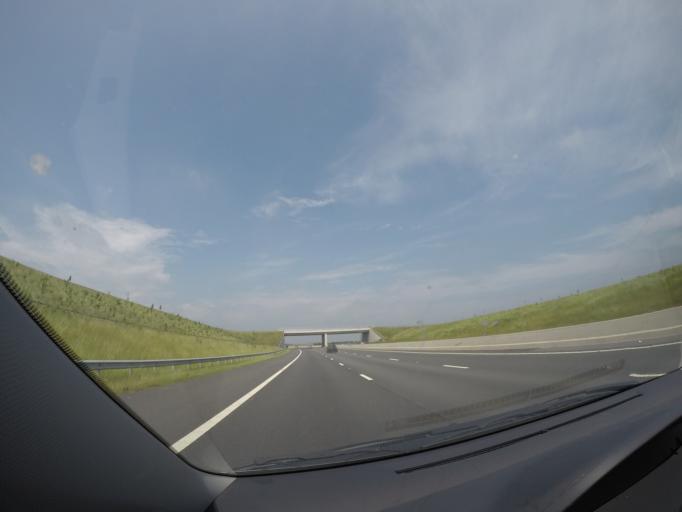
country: GB
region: England
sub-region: North Yorkshire
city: Catterick
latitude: 54.3683
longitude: -1.6350
